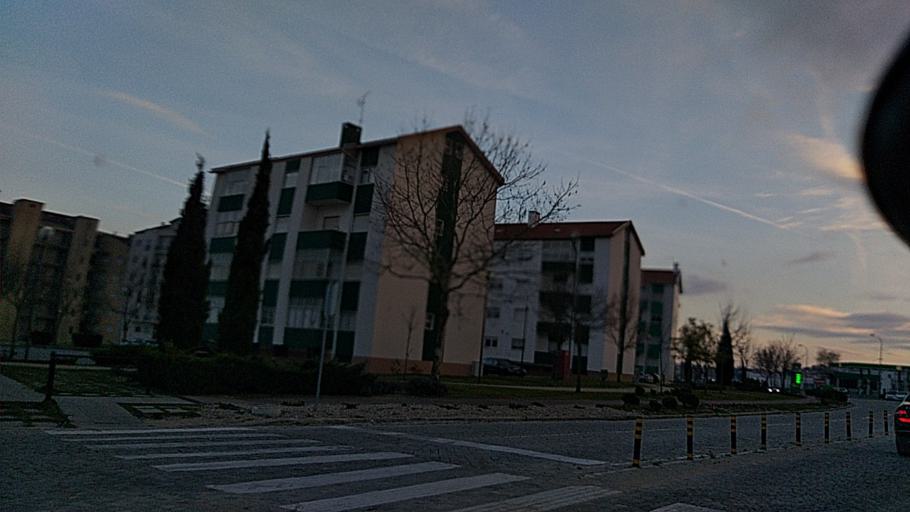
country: PT
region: Guarda
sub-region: Guarda
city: Sequeira
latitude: 40.5546
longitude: -7.2460
